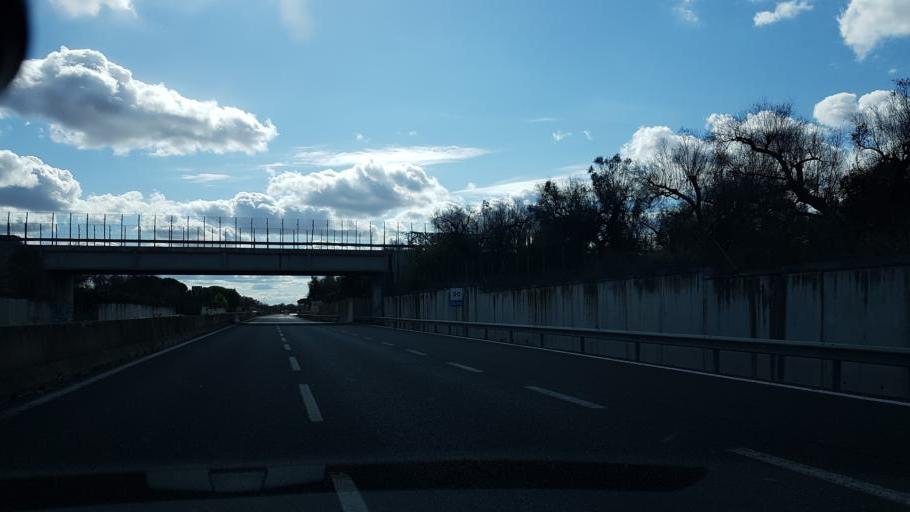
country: IT
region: Apulia
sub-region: Provincia di Brindisi
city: Torchiarolo
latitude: 40.4638
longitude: 18.0569
